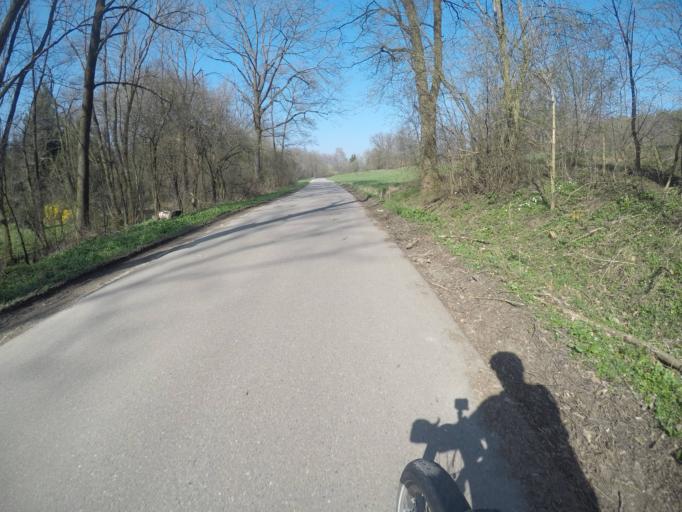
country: DE
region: Baden-Wuerttemberg
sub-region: Tuebingen Region
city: Pliezhausen
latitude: 48.5719
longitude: 9.2102
